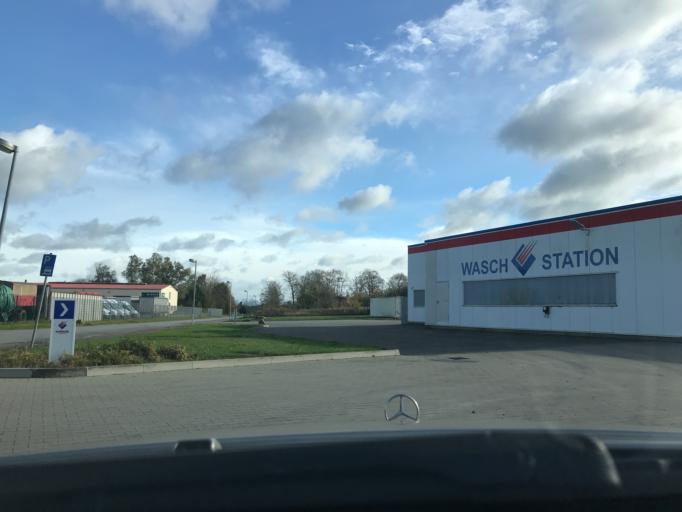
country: DE
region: Mecklenburg-Vorpommern
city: Jarmen
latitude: 53.9439
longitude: 13.3960
